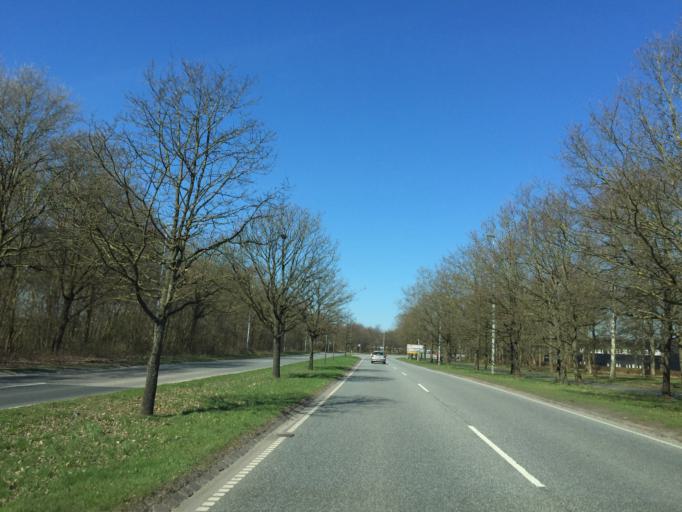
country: DK
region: South Denmark
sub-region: Odense Kommune
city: Neder Holluf
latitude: 55.3749
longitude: 10.4393
